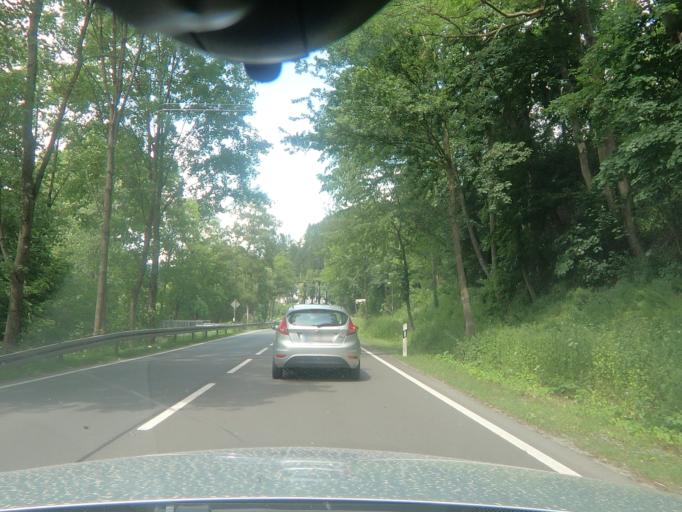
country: DE
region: North Rhine-Westphalia
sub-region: Regierungsbezirk Arnsberg
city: Olsberg
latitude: 51.3117
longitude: 8.5037
